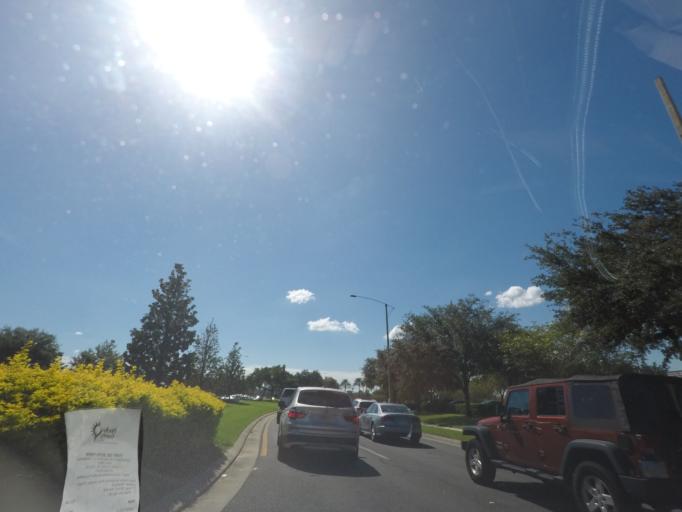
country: US
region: Florida
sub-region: Orange County
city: Oak Ridge
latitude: 28.4868
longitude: -81.4268
